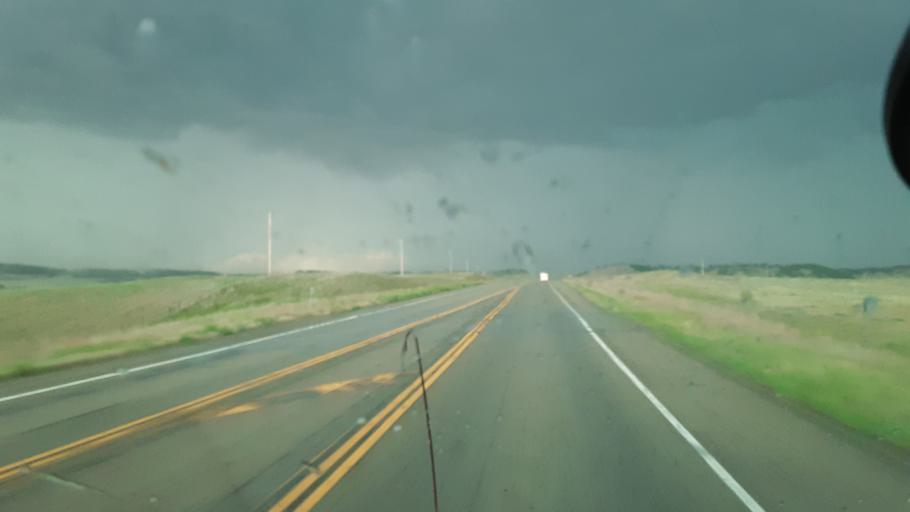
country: US
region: Montana
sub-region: Powder River County
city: Broadus
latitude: 45.4666
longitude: -105.4657
